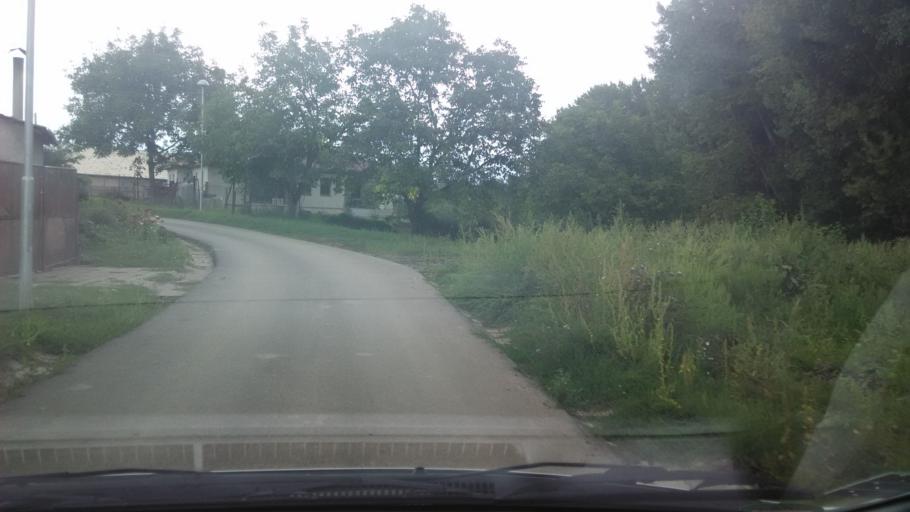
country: SK
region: Nitriansky
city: Levice
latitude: 48.1935
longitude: 18.5226
